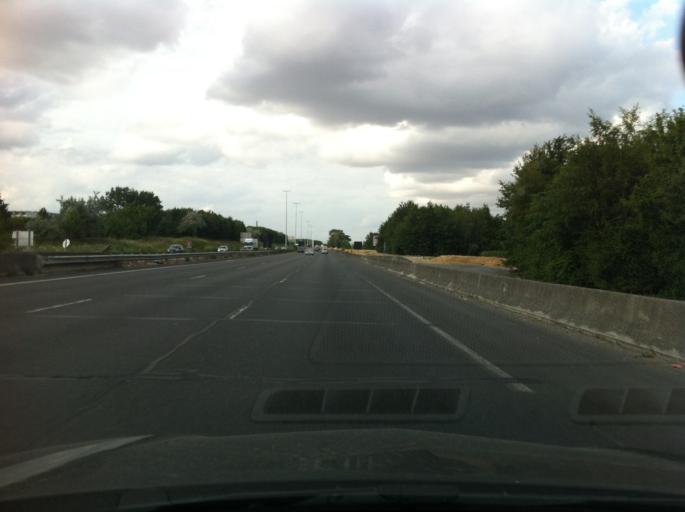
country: FR
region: Ile-de-France
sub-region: Departement du Val-d'Oise
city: Roissy-en-France
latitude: 48.9951
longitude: 2.5164
